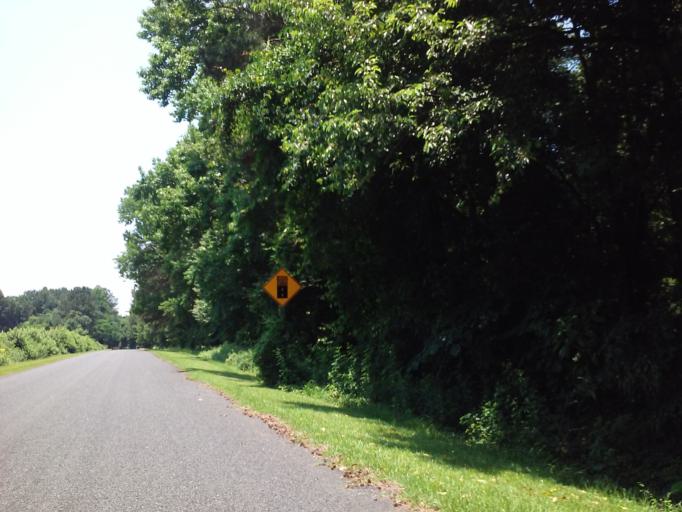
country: US
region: North Carolina
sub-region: Wake County
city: Fuquay-Varina
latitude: 35.5408
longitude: -78.8776
